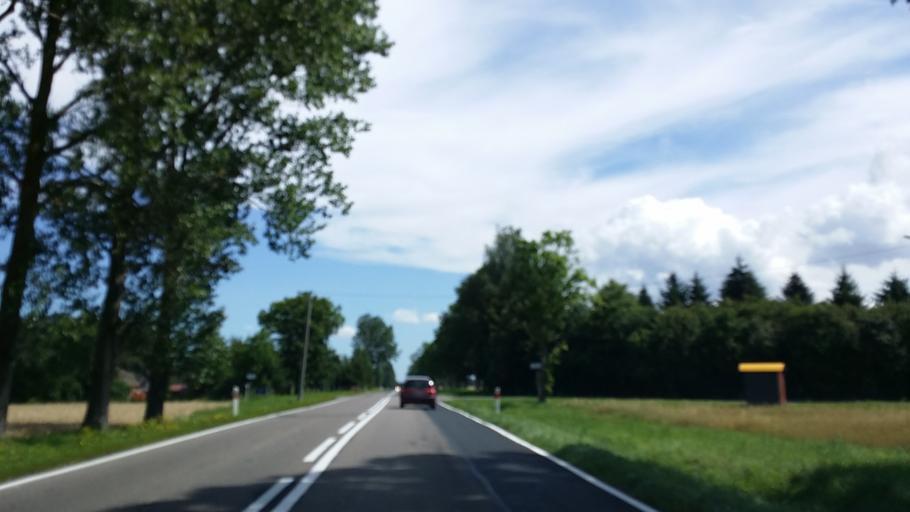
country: PL
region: West Pomeranian Voivodeship
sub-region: Powiat koszalinski
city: Mielno
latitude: 54.2085
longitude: 15.9642
